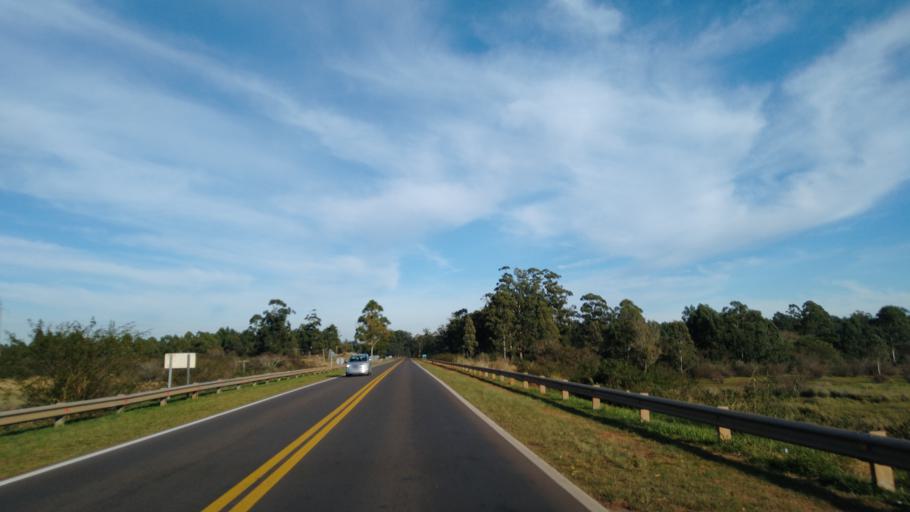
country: AR
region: Corrientes
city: Yapeyu
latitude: -29.4236
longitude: -56.8544
